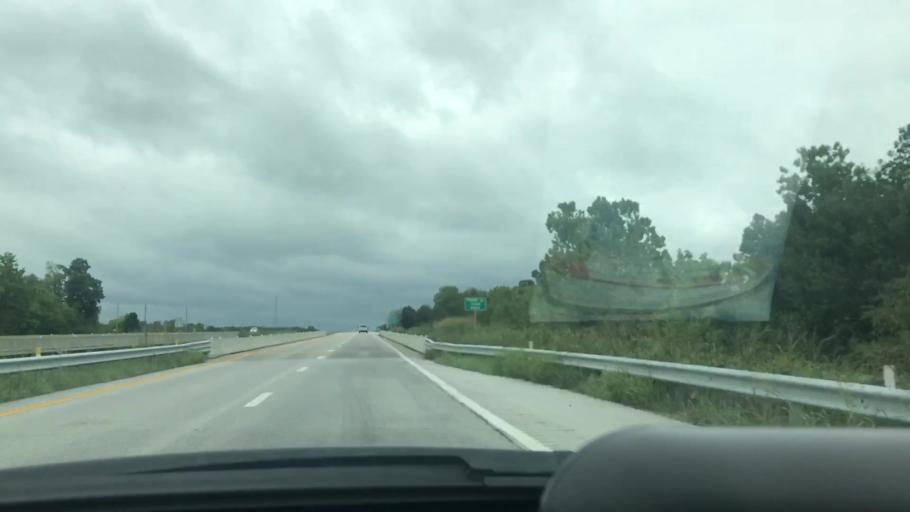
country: US
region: Missouri
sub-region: Greene County
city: Fair Grove
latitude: 37.4150
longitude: -93.1452
